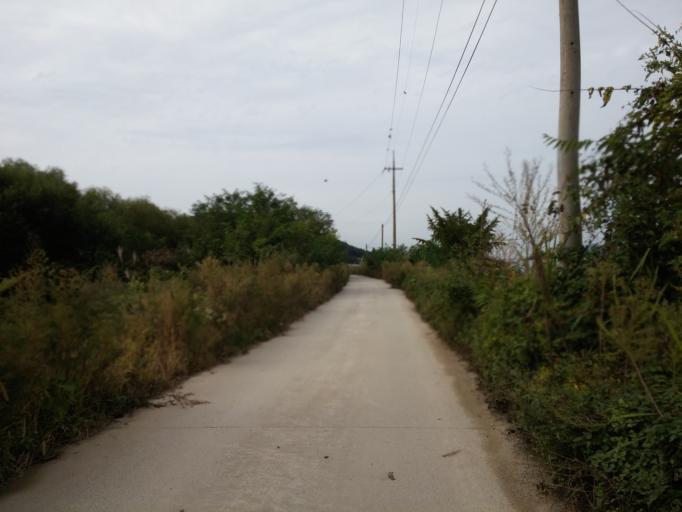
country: KR
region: Chungcheongnam-do
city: Yonmu
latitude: 36.1575
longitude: 127.2029
